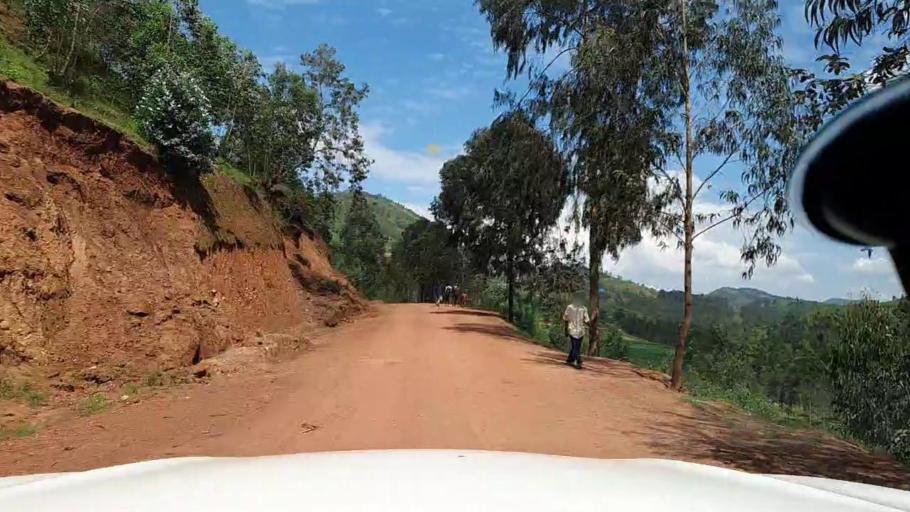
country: RW
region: Kigali
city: Kigali
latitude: -1.7787
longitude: 29.8764
